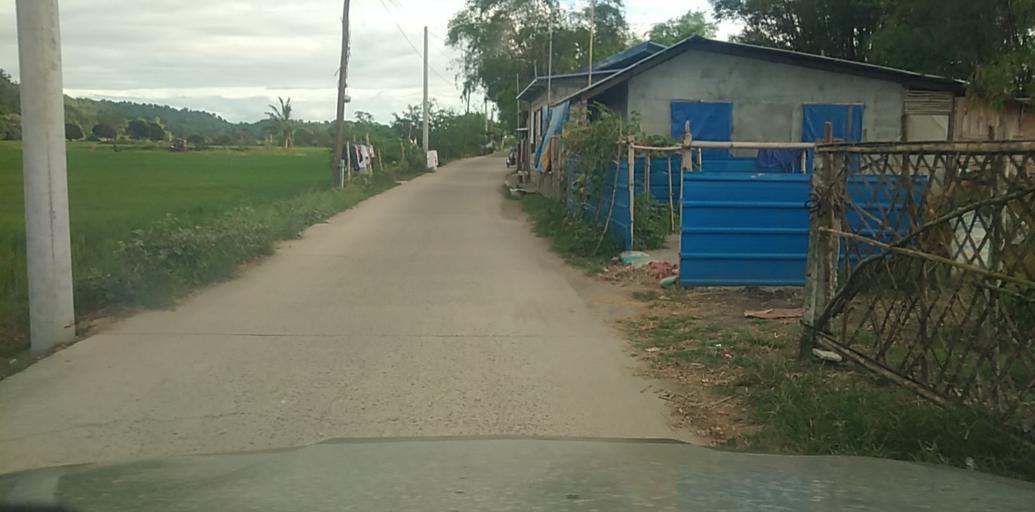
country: PH
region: Central Luzon
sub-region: Province of Pampanga
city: Panlinlang
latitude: 15.1810
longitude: 120.6993
